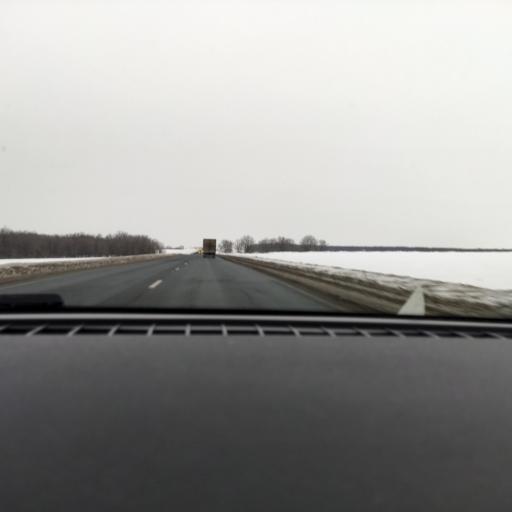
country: RU
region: Samara
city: Petra-Dubrava
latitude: 53.3192
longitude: 50.4560
